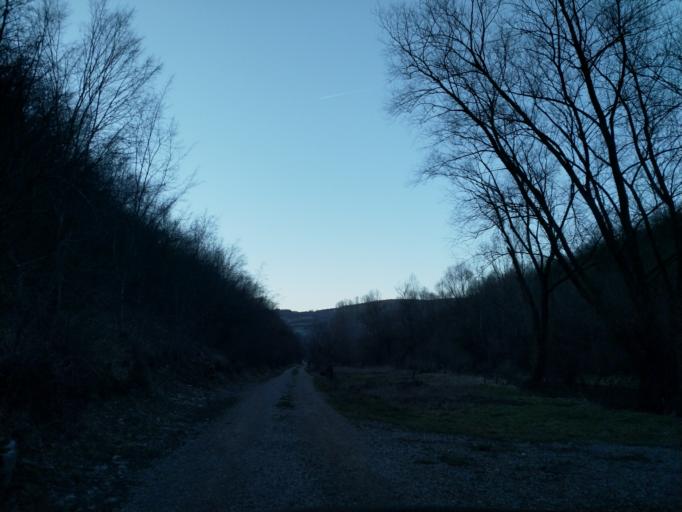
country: RS
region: Central Serbia
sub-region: Pomoravski Okrug
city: Paracin
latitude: 43.9264
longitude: 21.5250
